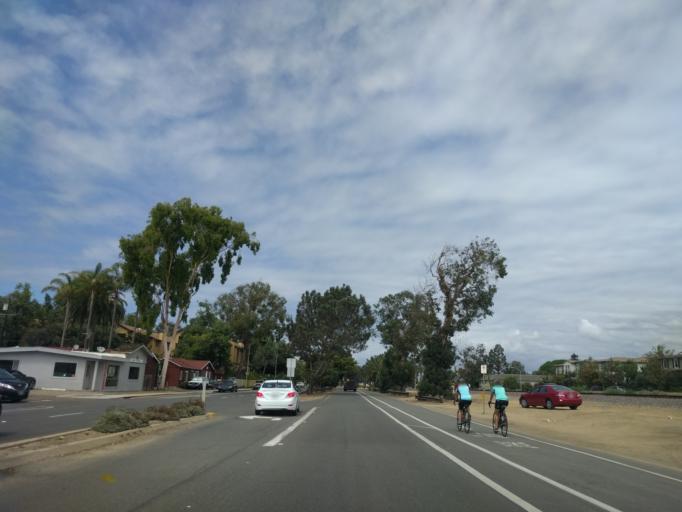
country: US
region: California
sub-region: San Diego County
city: Encinitas
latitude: 33.0761
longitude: -117.3061
